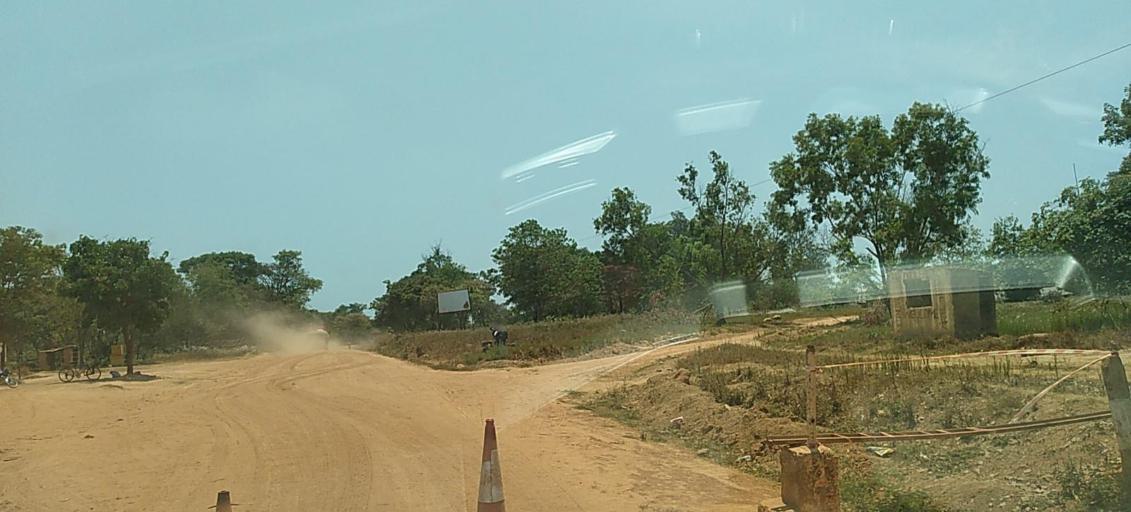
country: CD
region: Katanga
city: Kipushi
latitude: -11.8579
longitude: 27.1188
